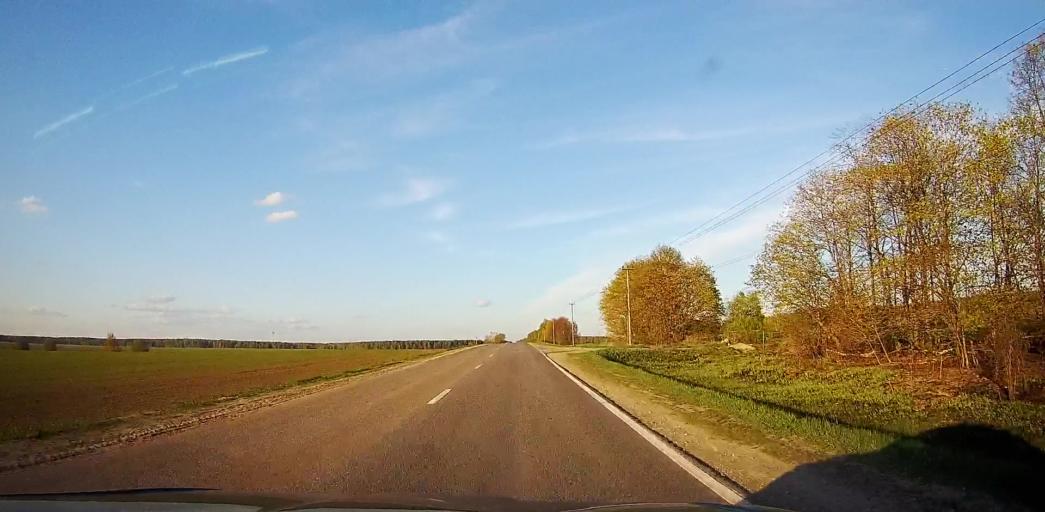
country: RU
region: Moskovskaya
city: Bronnitsy
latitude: 55.2850
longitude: 38.1802
